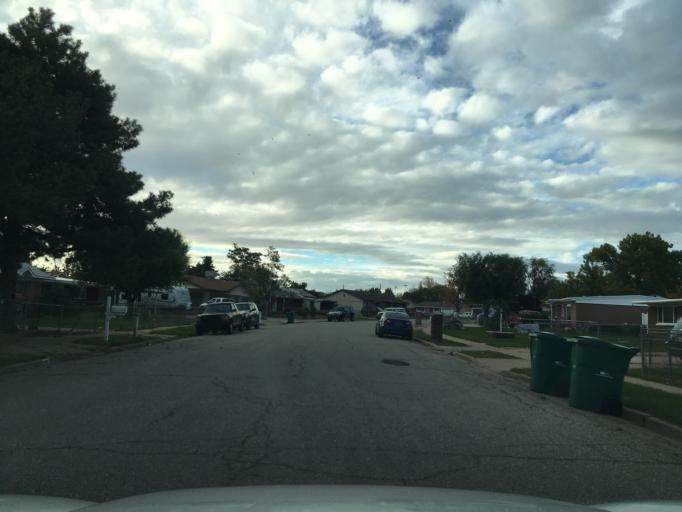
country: US
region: Utah
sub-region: Davis County
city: Layton
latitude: 41.0806
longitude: -111.9939
